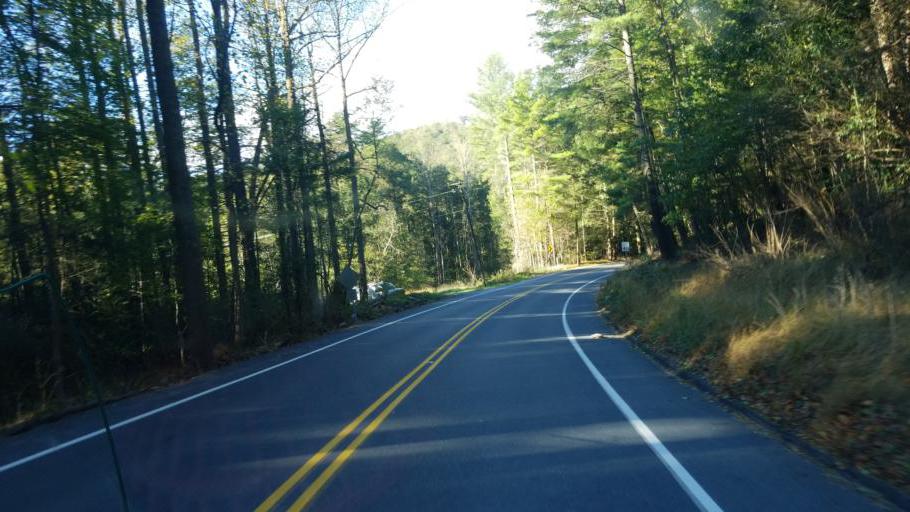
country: US
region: Pennsylvania
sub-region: Franklin County
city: Mont Alto
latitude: 39.8374
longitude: -77.5285
